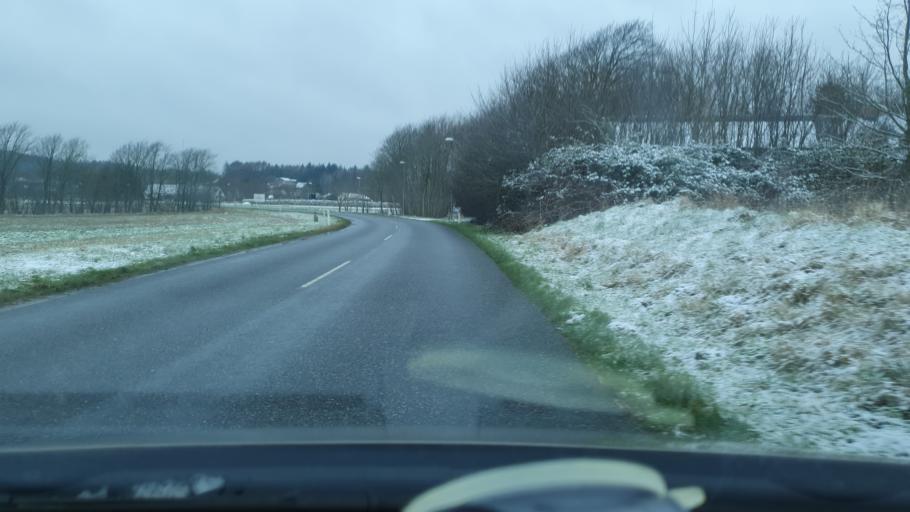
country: DK
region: North Denmark
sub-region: Jammerbugt Kommune
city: Brovst
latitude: 57.1307
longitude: 9.4714
